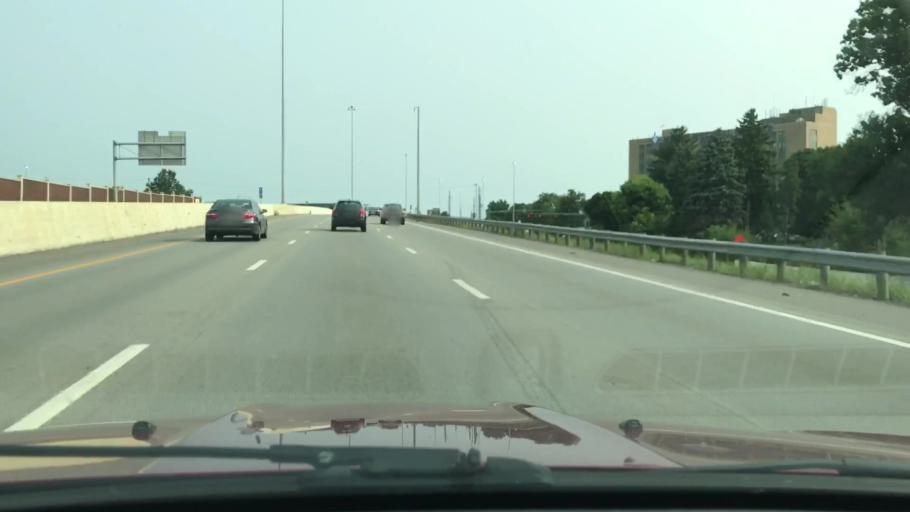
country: US
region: Ohio
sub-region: Stark County
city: Canton
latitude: 40.8097
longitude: -81.3976
